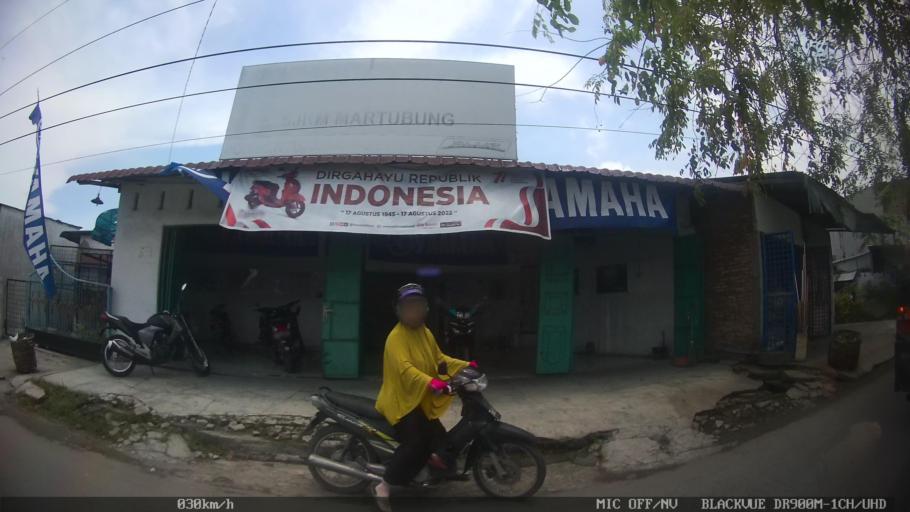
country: ID
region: North Sumatra
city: Labuhan Deli
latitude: 3.6822
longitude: 98.6888
